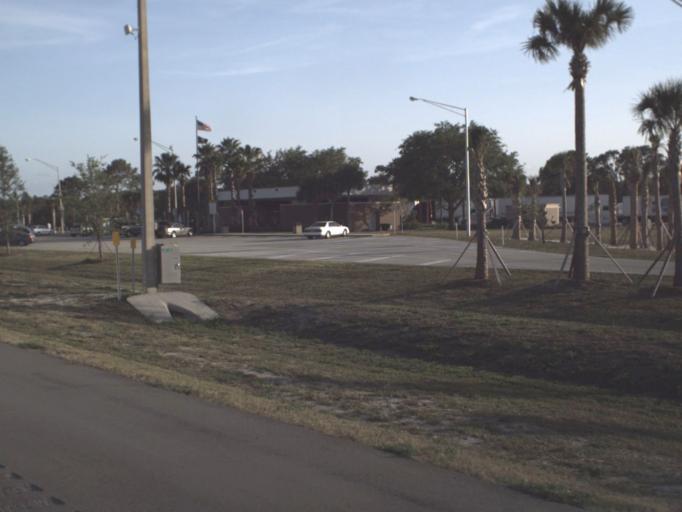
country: US
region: Florida
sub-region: Brevard County
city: Mims
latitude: 28.7097
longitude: -80.8877
